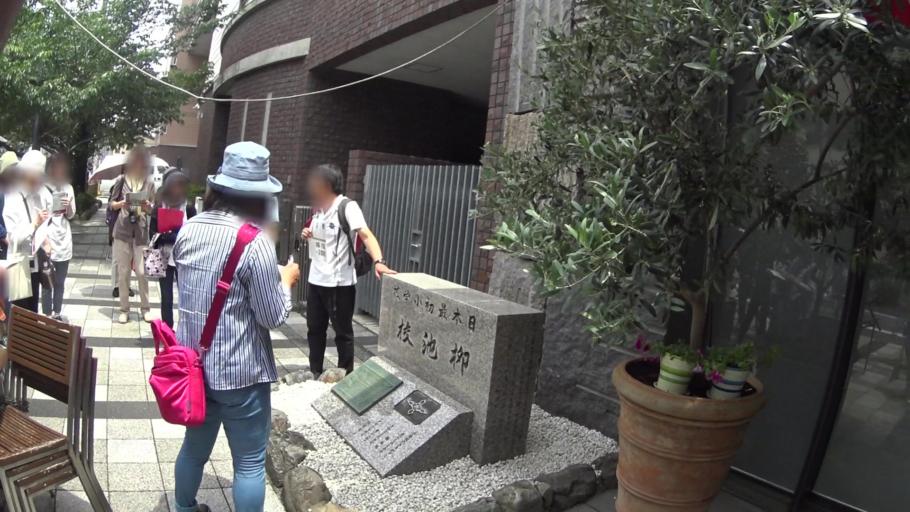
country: JP
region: Kyoto
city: Kyoto
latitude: 35.0104
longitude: 135.7643
